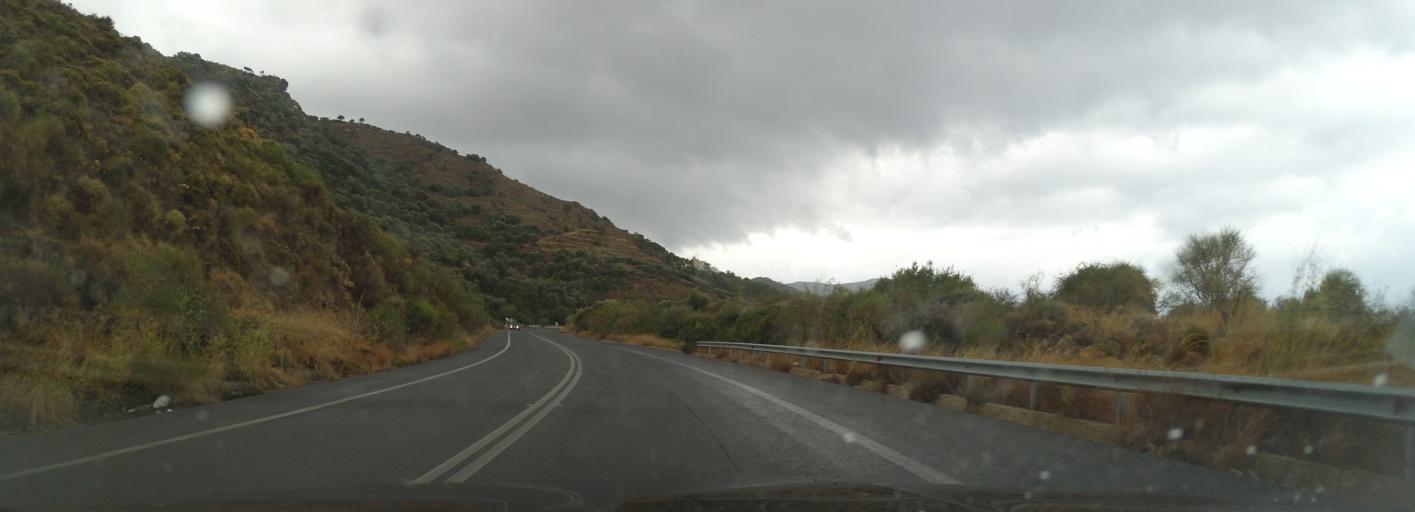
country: GR
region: Crete
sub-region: Nomos Irakleiou
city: Gazi
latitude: 35.4000
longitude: 25.0100
